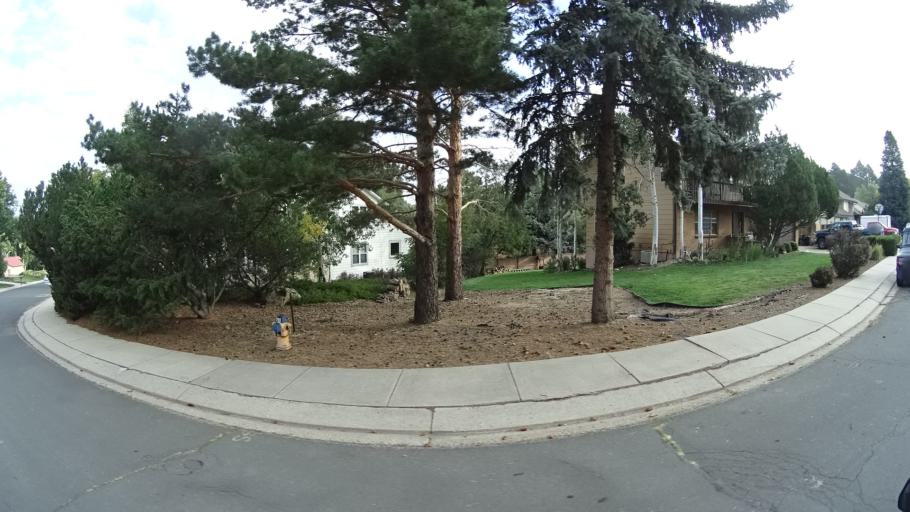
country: US
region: Colorado
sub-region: El Paso County
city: Cimarron Hills
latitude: 38.8691
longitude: -104.7493
